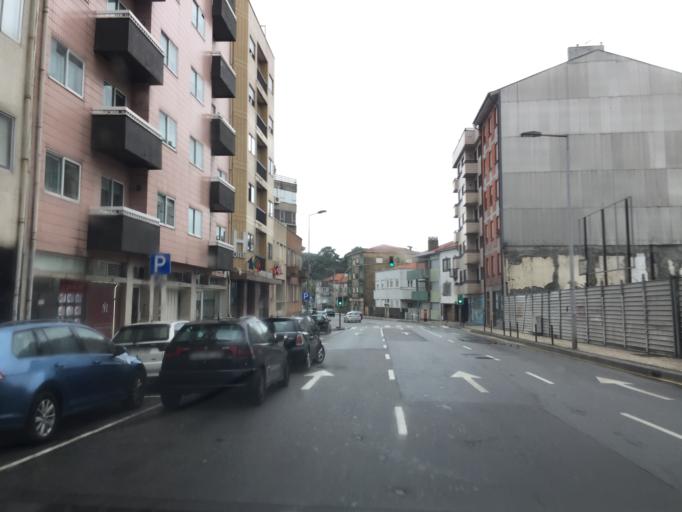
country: PT
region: Porto
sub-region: Porto
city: Porto
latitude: 41.1634
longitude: -8.6064
